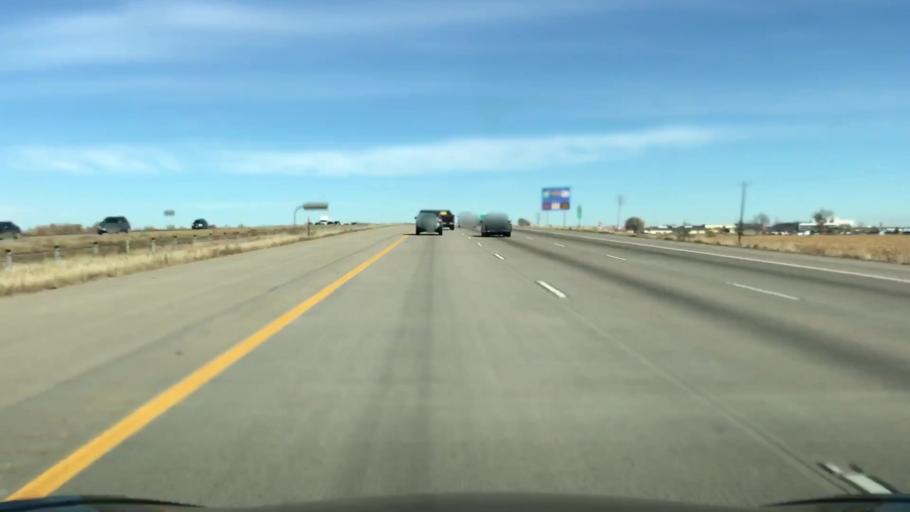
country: US
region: Colorado
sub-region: Weld County
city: Mead
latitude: 40.1868
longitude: -104.9800
